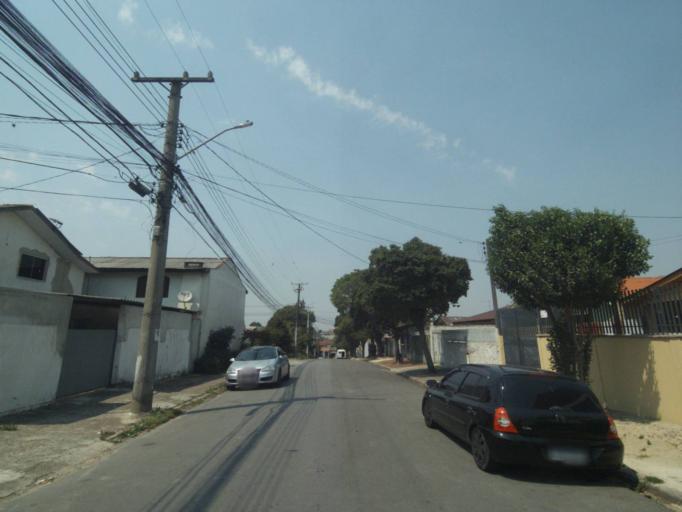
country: BR
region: Parana
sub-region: Sao Jose Dos Pinhais
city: Sao Jose dos Pinhais
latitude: -25.5312
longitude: -49.2483
